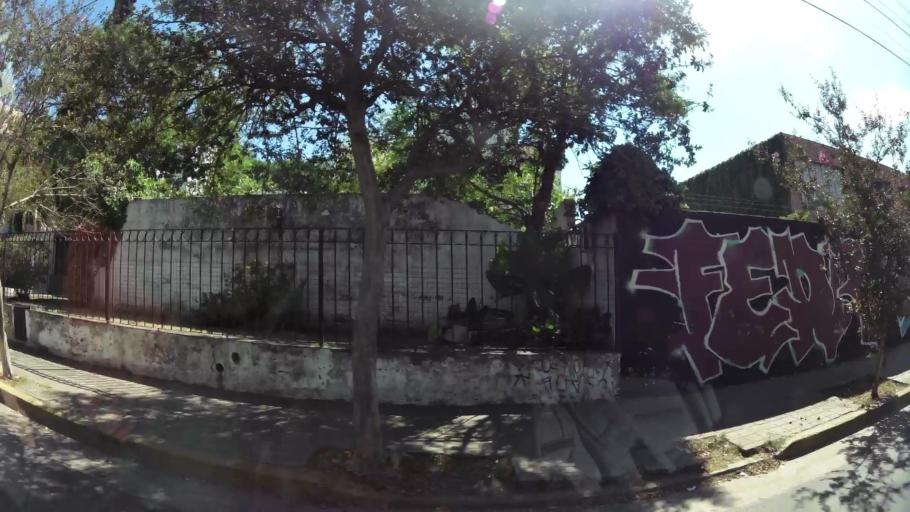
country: AR
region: Cordoba
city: Villa Allende
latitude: -31.2927
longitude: -64.2979
